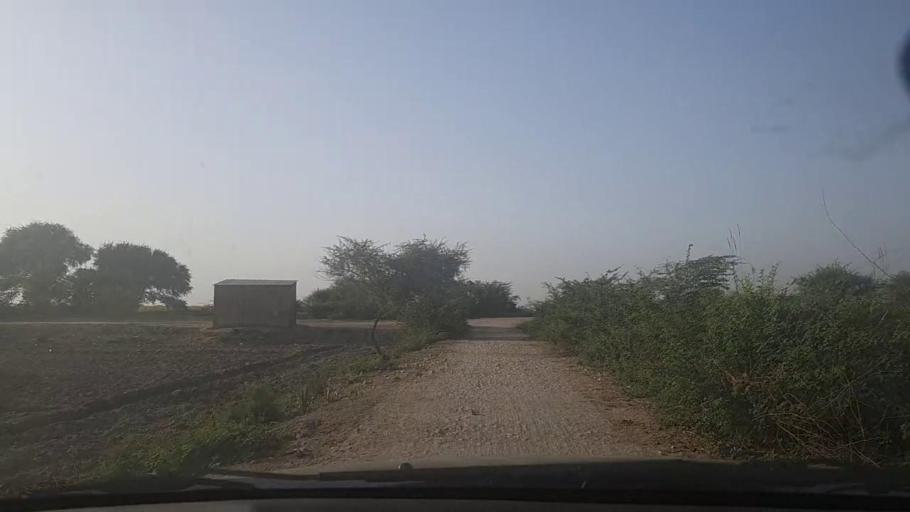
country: PK
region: Sindh
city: Keti Bandar
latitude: 24.2775
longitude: 67.5958
